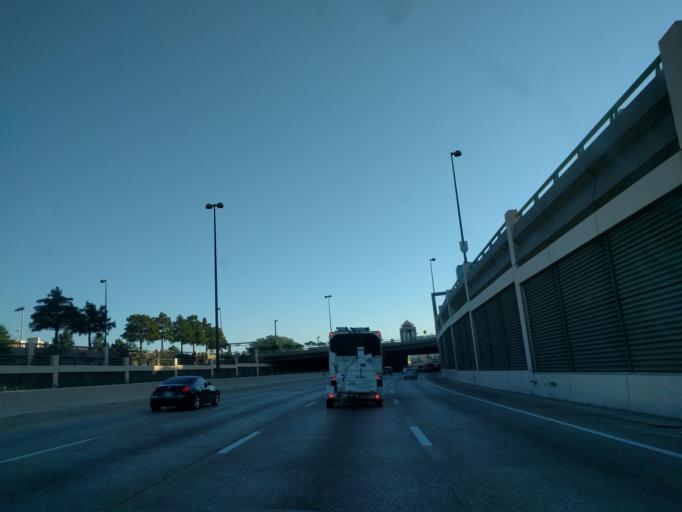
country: US
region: Texas
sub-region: Dallas County
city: Highland Park
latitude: 32.8352
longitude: -96.7794
